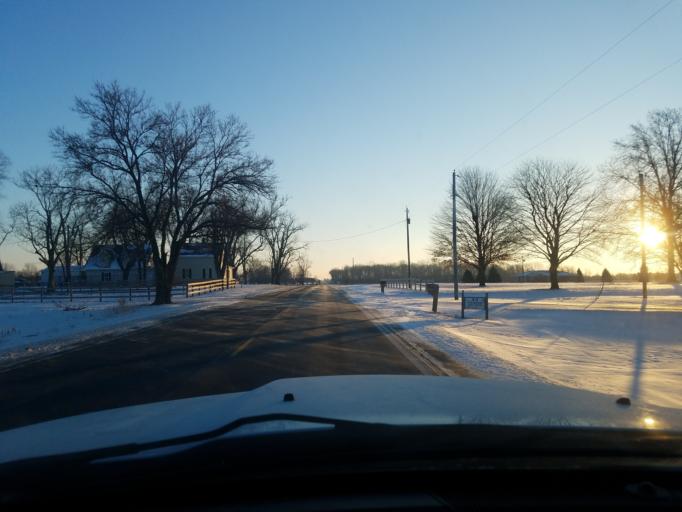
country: US
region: Indiana
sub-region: Marshall County
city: Plymouth
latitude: 41.4496
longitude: -86.2700
